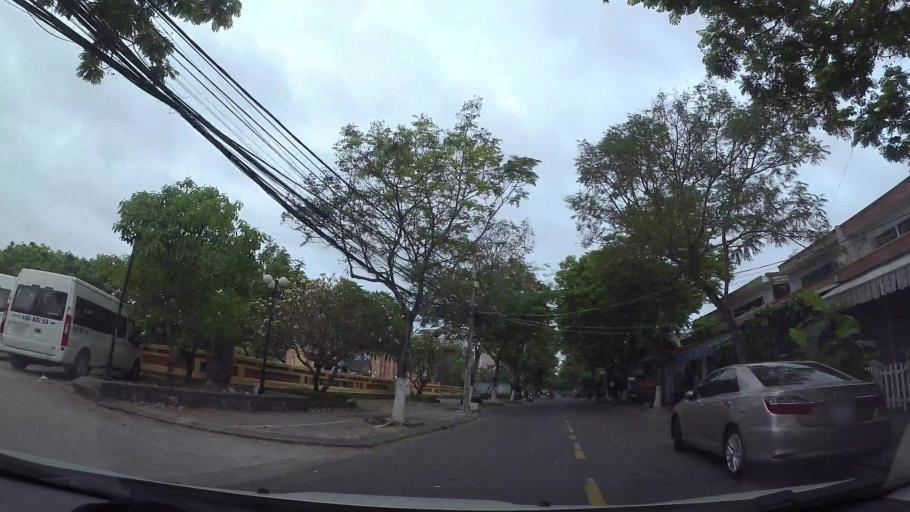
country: VN
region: Da Nang
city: Son Tra
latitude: 16.0588
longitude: 108.2313
